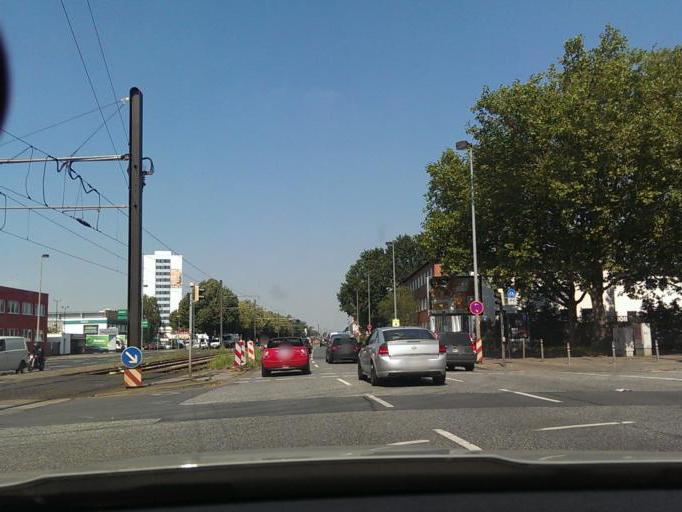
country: DE
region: Lower Saxony
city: Hannover
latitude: 52.4034
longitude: 9.7355
